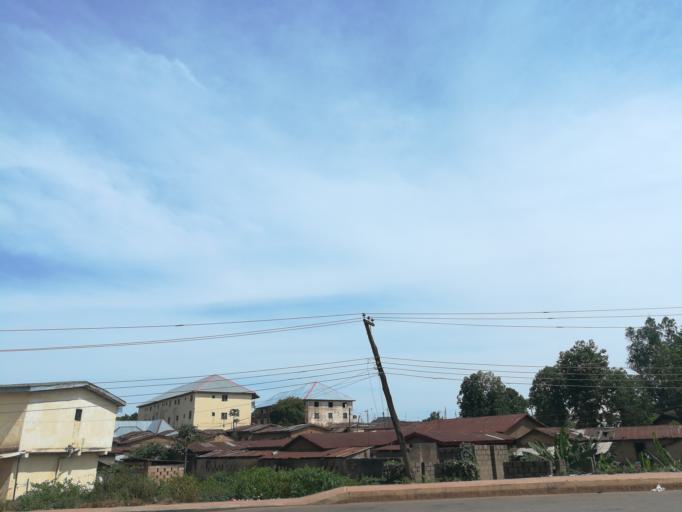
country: NG
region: Plateau
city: Bukuru
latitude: 9.7880
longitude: 8.8588
